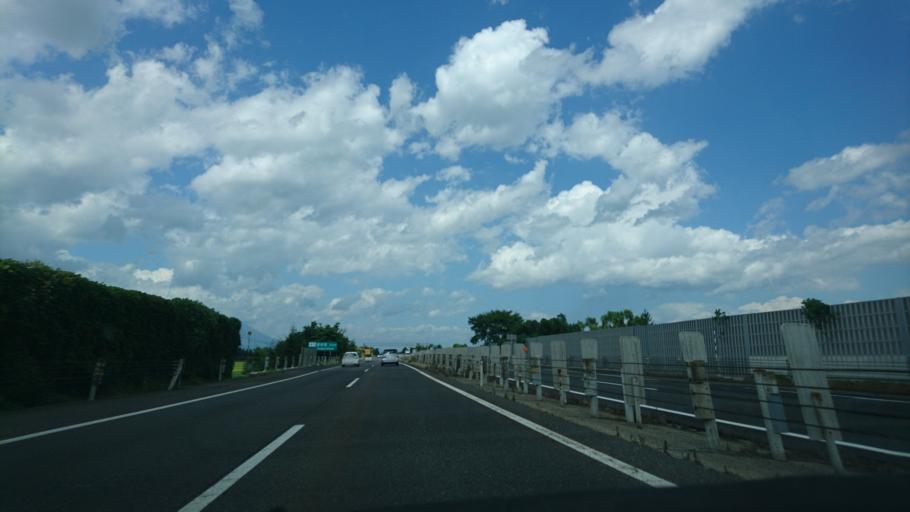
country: JP
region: Iwate
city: Morioka-shi
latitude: 39.6313
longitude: 141.1276
